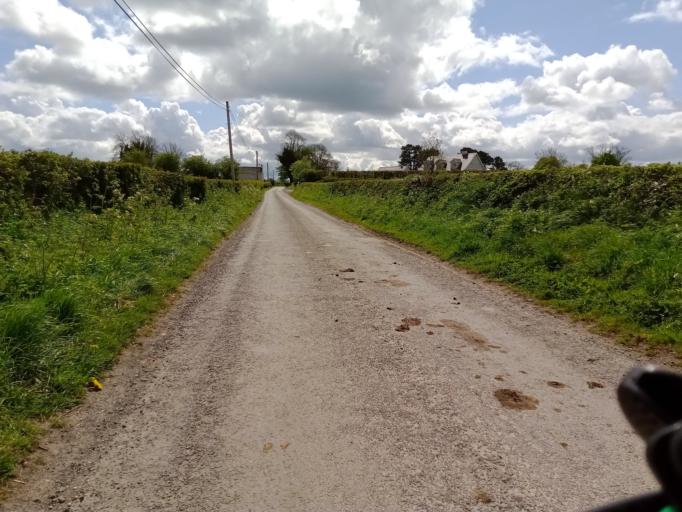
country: IE
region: Leinster
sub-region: Kilkenny
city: Thomastown
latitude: 52.5915
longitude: -7.1474
